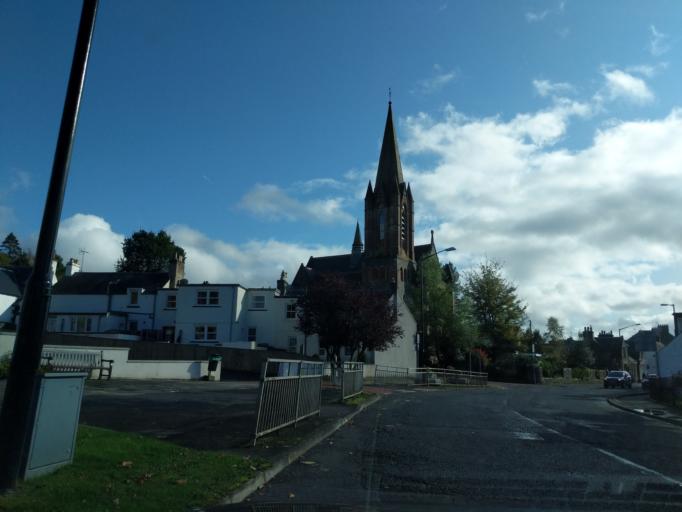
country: GB
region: Scotland
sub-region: Dumfries and Galloway
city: Moffat
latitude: 55.3359
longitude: -3.4460
